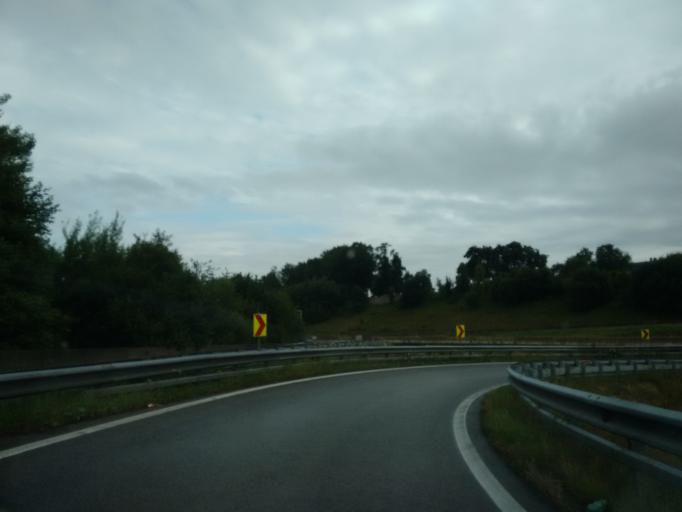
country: AT
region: Upper Austria
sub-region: Wels-Land
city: Sattledt
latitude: 48.0680
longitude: 14.0292
